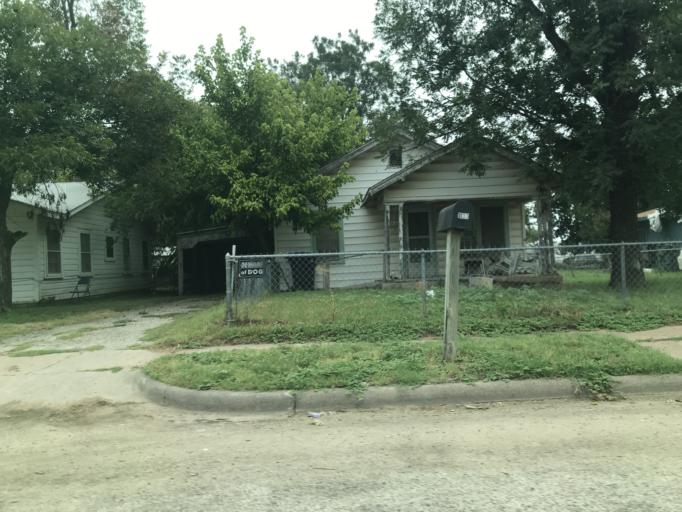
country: US
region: Texas
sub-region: Taylor County
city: Abilene
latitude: 32.4367
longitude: -99.7363
